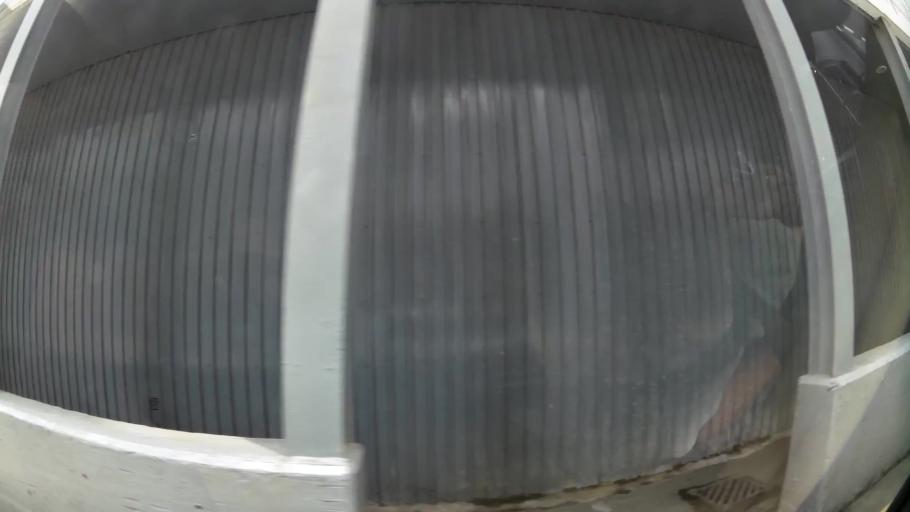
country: HK
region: Wanchai
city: Wan Chai
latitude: 22.2873
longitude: 114.2126
